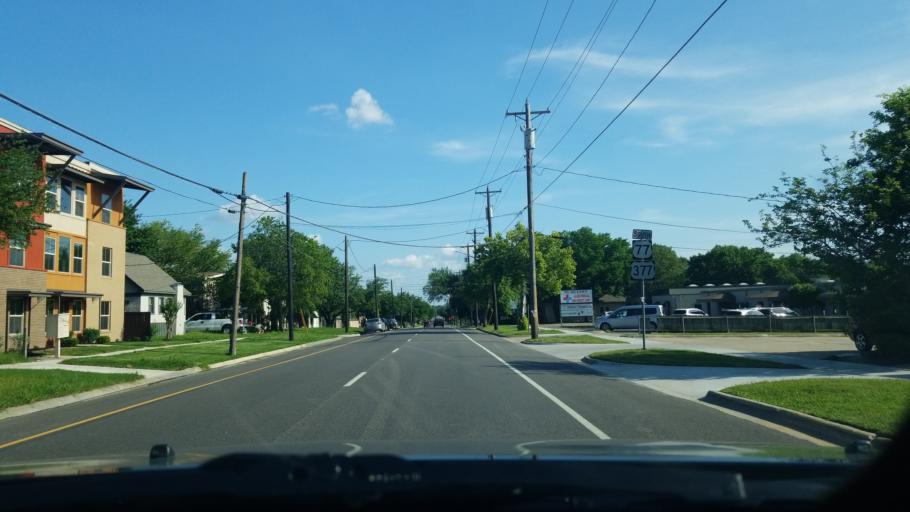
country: US
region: Texas
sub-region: Denton County
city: Denton
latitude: 33.2277
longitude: -97.1336
